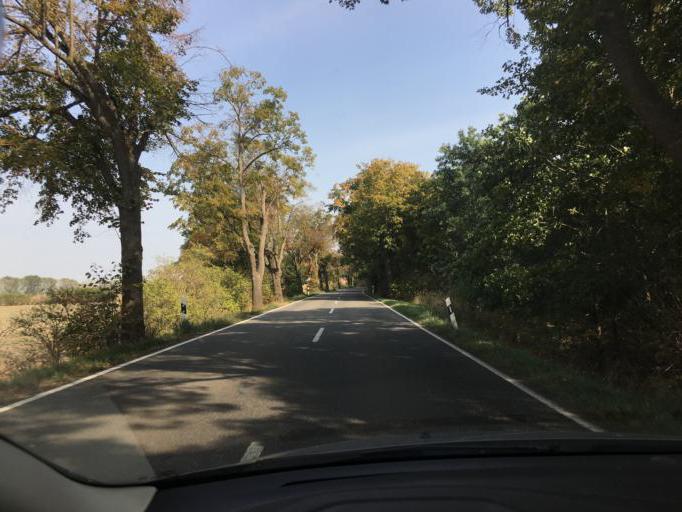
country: DE
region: Saxony-Anhalt
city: Nienburg/Saale
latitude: 51.8456
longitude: 11.7838
